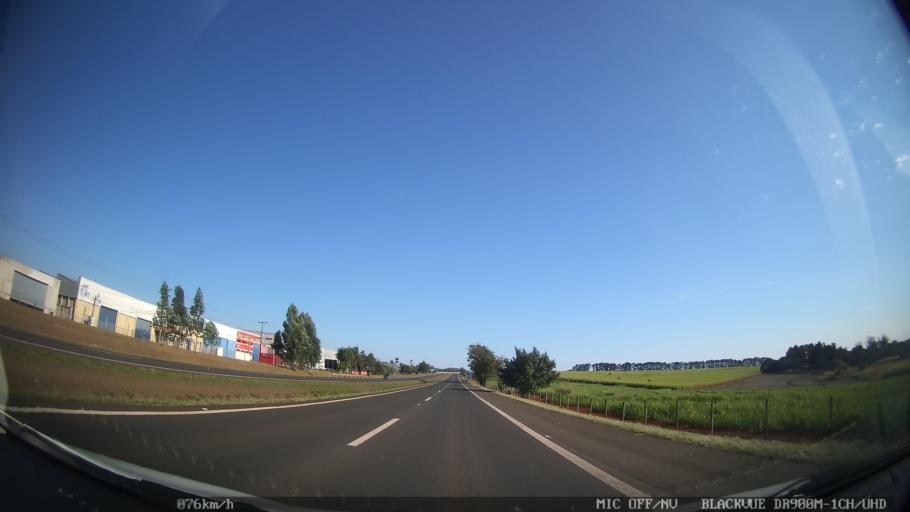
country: BR
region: Sao Paulo
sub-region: Piracicaba
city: Piracicaba
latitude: -22.6827
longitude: -47.6372
